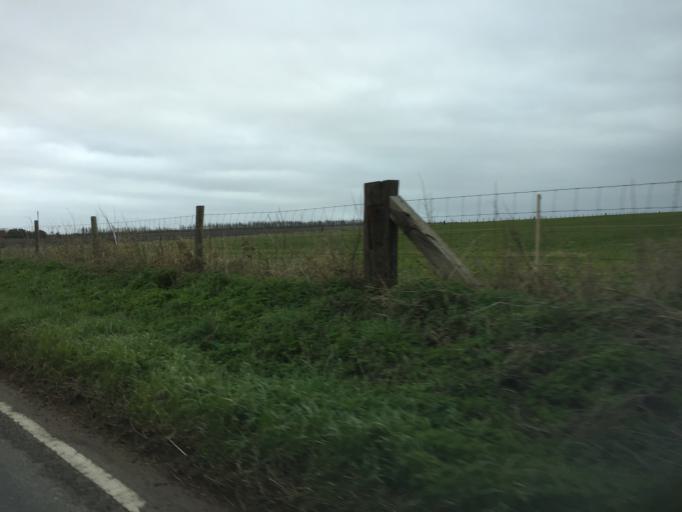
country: GB
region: England
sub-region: Oxfordshire
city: Harwell
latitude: 51.5942
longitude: -1.2873
